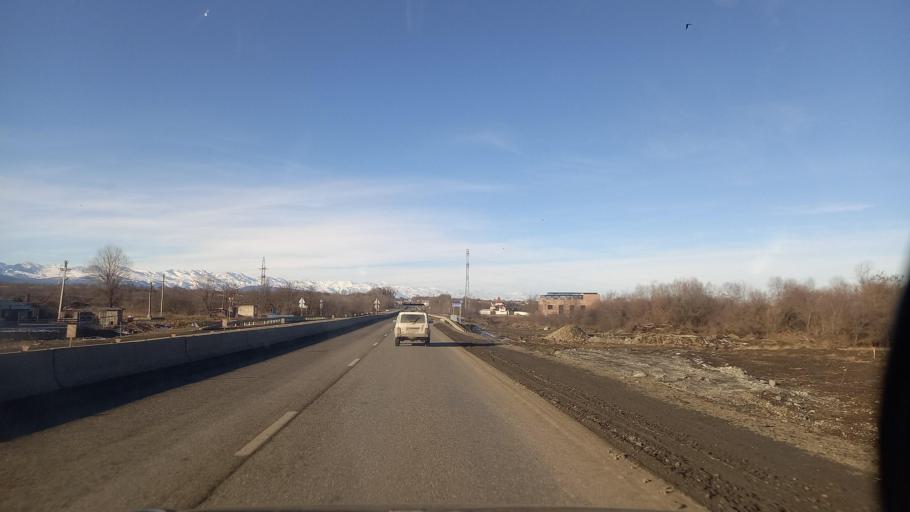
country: RU
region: North Ossetia
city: Gizel'
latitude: 43.0279
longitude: 44.6025
